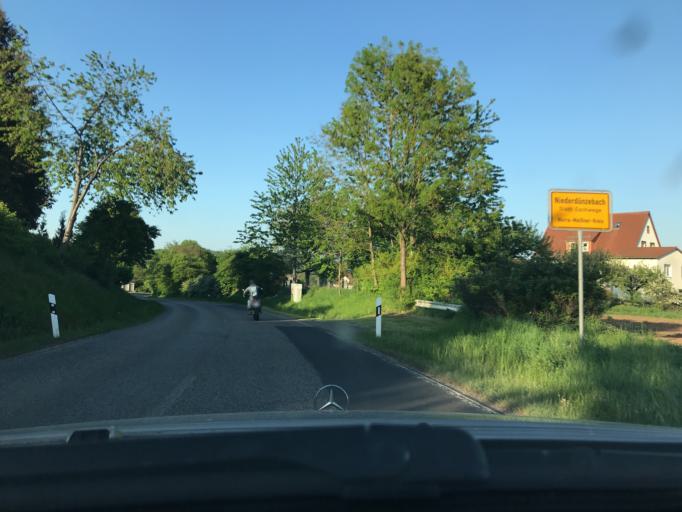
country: DE
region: Hesse
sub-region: Regierungsbezirk Kassel
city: Eschwege
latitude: 51.1777
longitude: 10.0898
